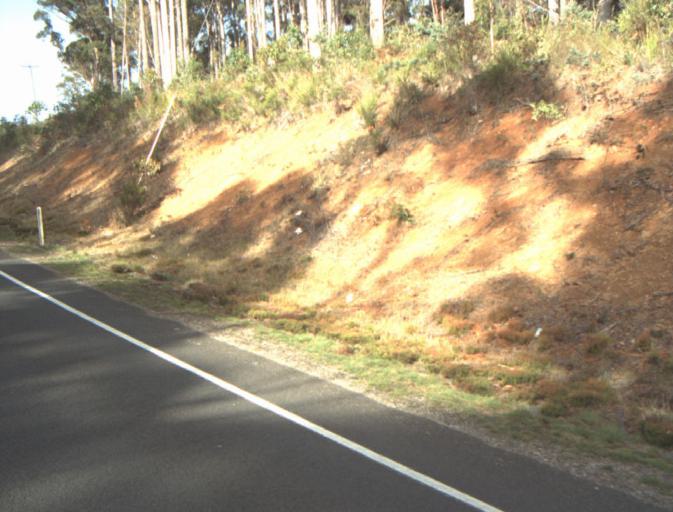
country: AU
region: Tasmania
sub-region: Launceston
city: Mayfield
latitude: -41.3075
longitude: 147.2041
